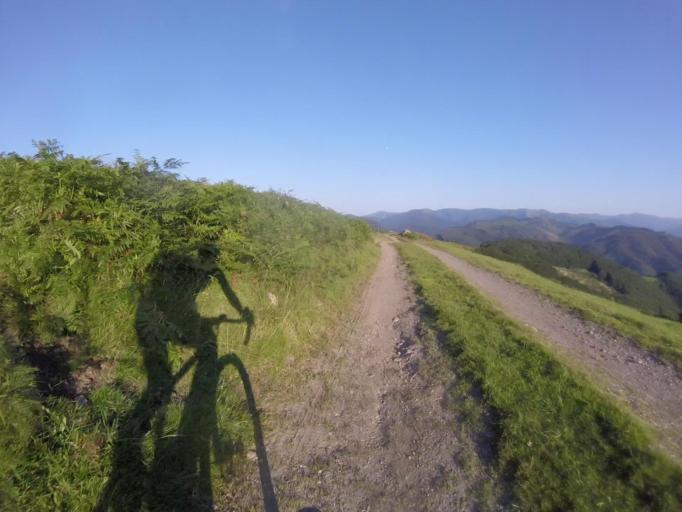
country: ES
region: Navarre
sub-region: Provincia de Navarra
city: Arano
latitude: 43.2421
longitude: -1.8427
